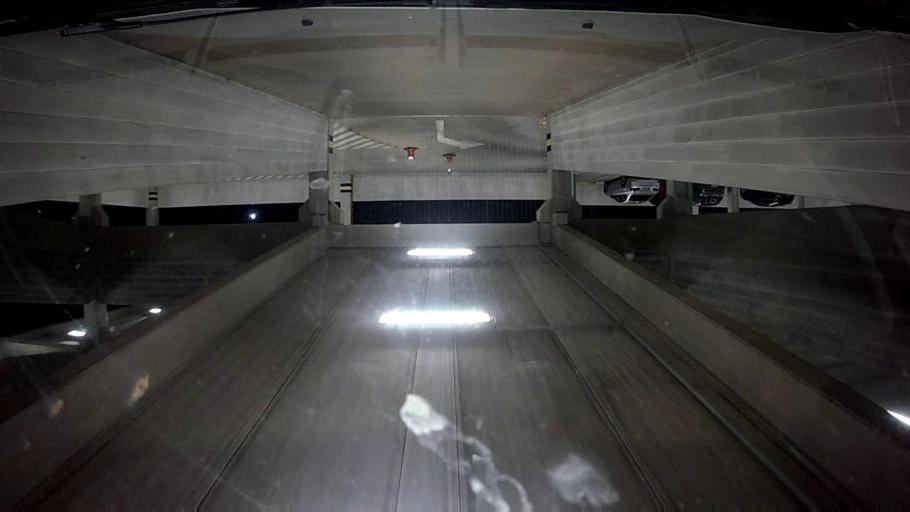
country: BR
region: Sao Paulo
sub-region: Louveira
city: Louveira
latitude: -23.1062
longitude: -47.0098
